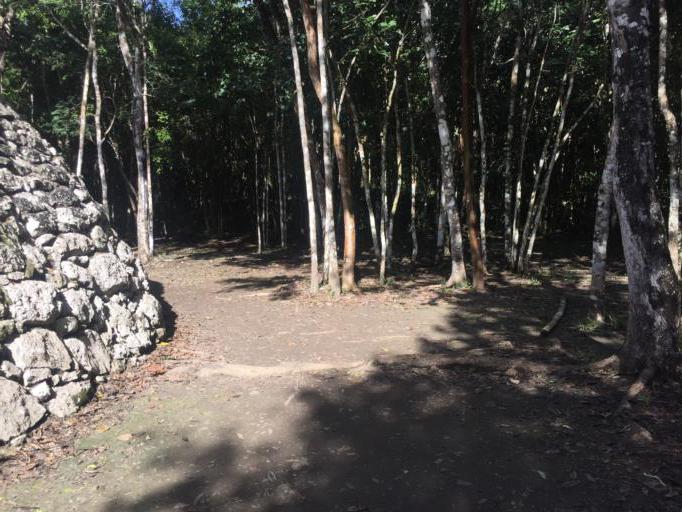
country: MX
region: Quintana Roo
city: Coba
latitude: 20.4932
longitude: -87.7217
